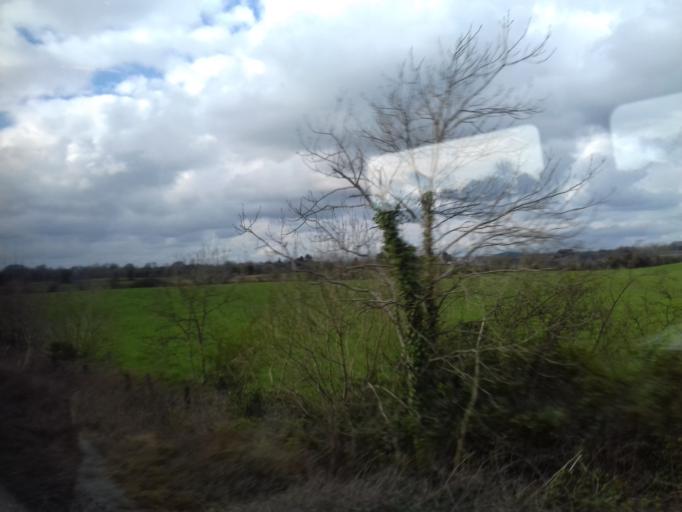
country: IE
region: Leinster
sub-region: An Iarmhi
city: An Muileann gCearr
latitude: 53.5048
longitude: -7.2821
